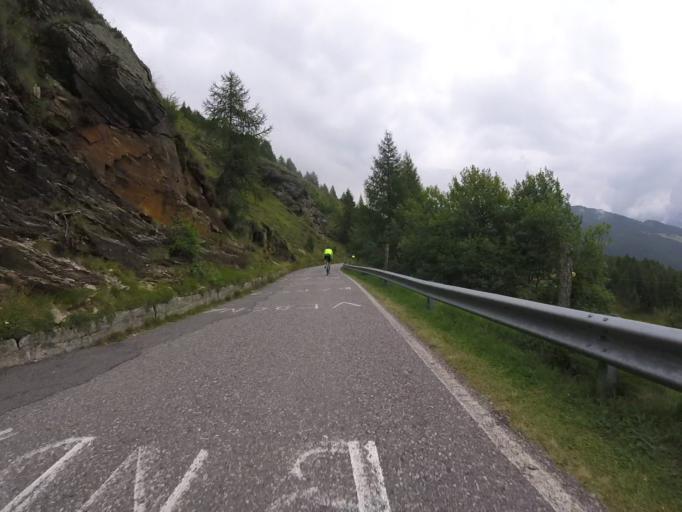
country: IT
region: Lombardy
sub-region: Provincia di Sondrio
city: Mazzo di Valtellina
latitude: 46.2483
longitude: 10.3033
